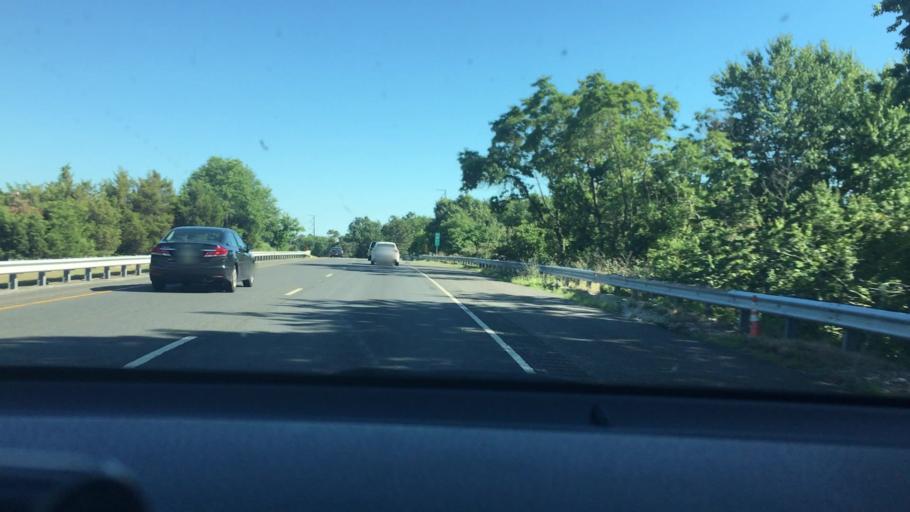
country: US
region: New Jersey
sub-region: Cumberland County
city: South Vineland
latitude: 39.4647
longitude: -75.0744
